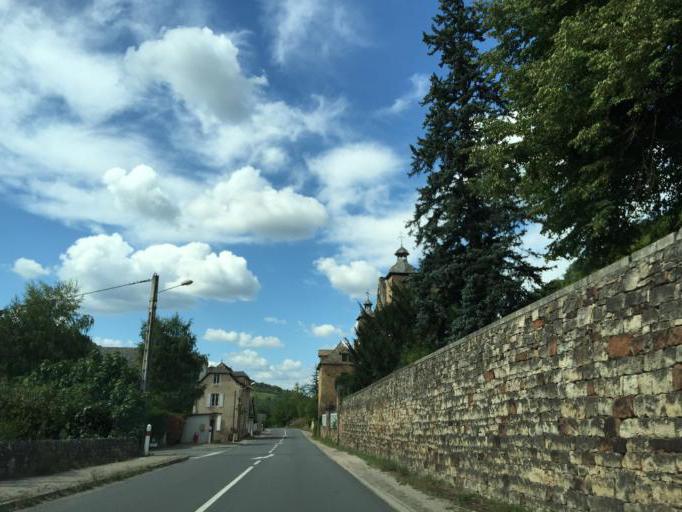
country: FR
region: Midi-Pyrenees
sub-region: Departement de l'Aveyron
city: Marcillac-Vallon
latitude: 44.4525
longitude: 2.4739
